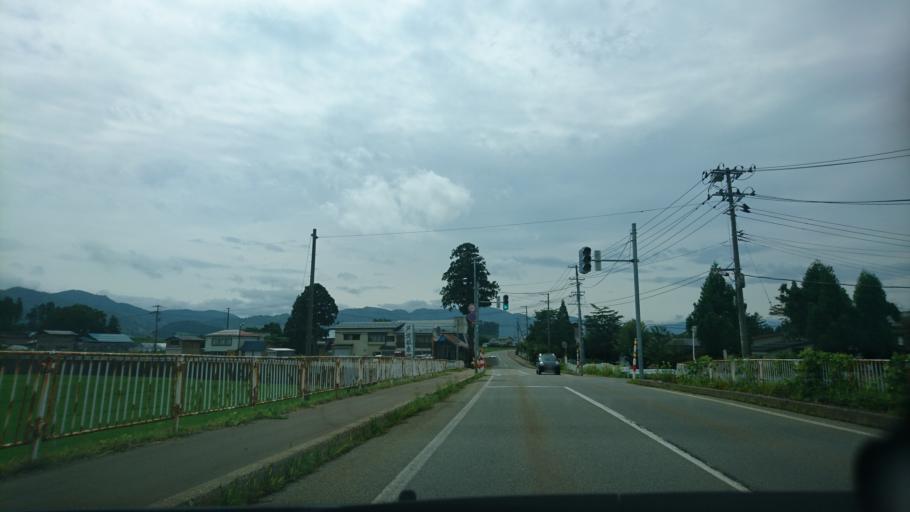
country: JP
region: Akita
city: Yuzawa
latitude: 39.1921
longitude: 140.5494
